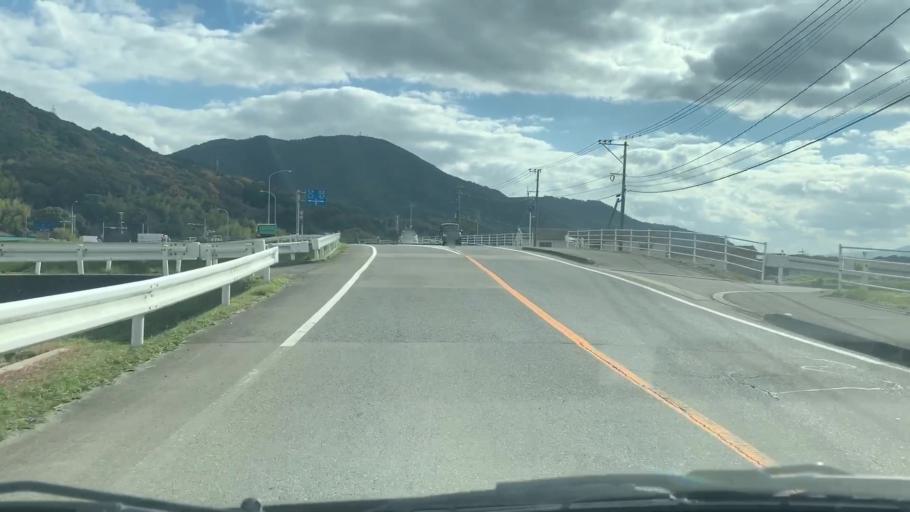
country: JP
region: Saga Prefecture
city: Takeocho-takeo
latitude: 33.2027
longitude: 130.0516
